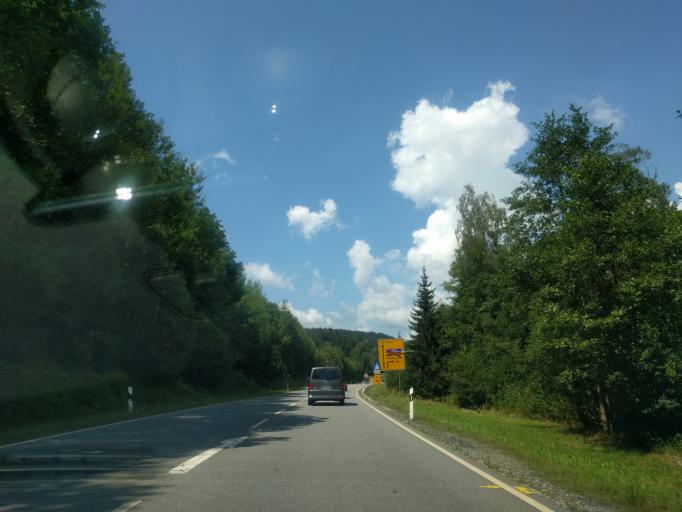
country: DE
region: Bavaria
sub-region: Lower Bavaria
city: Innernzell
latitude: 48.8451
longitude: 13.3107
